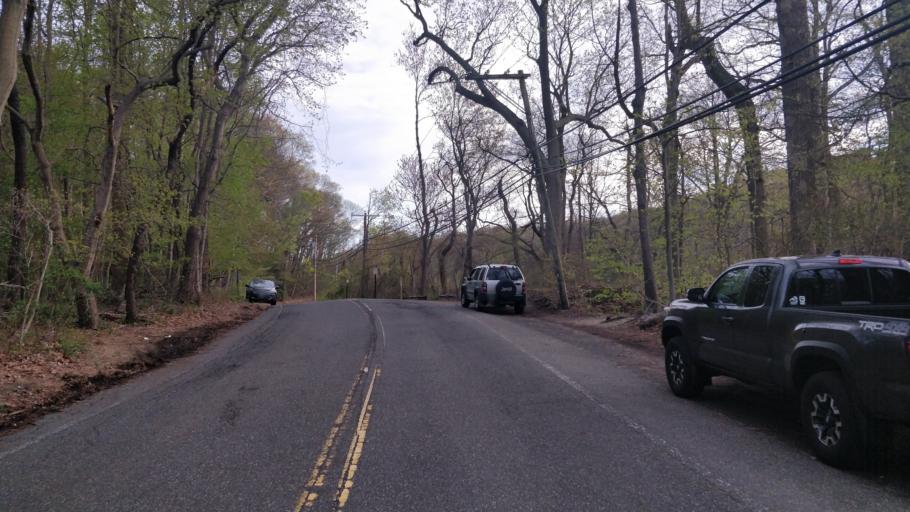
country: US
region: New York
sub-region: Suffolk County
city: Fort Salonga
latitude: 40.9167
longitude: -73.3112
